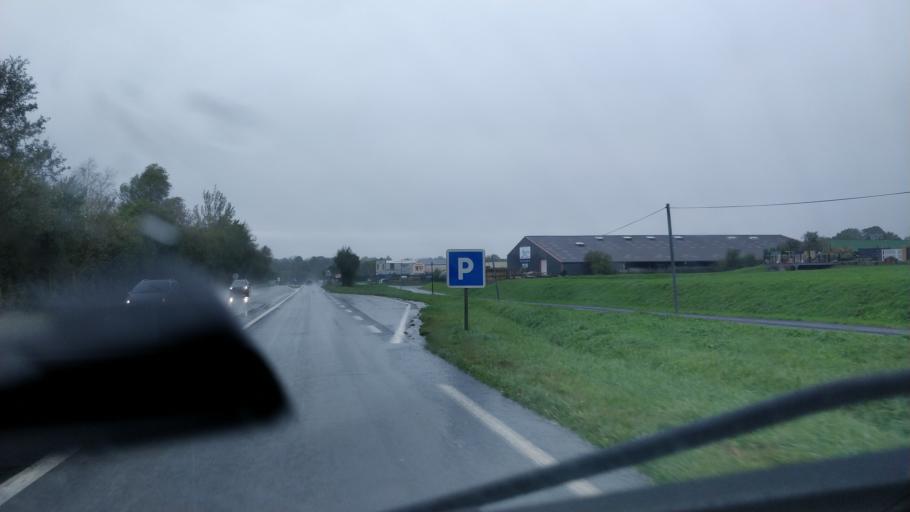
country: FR
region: Lower Normandy
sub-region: Departement de la Manche
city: Saint-Planchers
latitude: 48.8571
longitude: -1.5383
